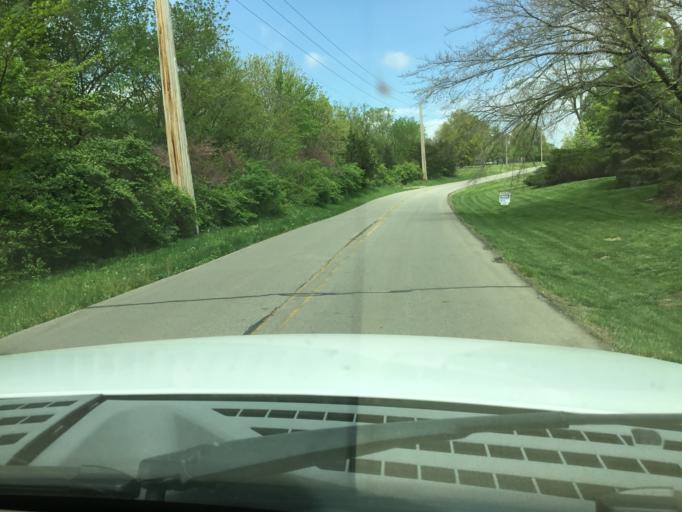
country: US
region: Kansas
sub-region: Shawnee County
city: Auburn
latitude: 39.0031
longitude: -95.8001
